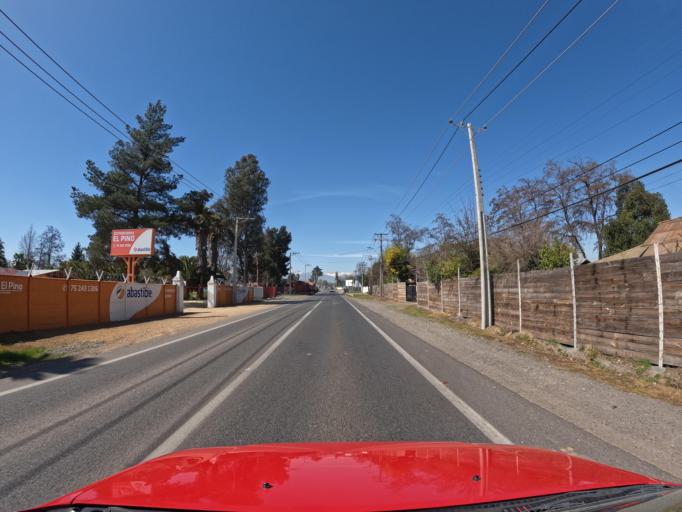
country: CL
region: Maule
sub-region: Provincia de Curico
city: Teno
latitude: -34.9612
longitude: -71.0965
